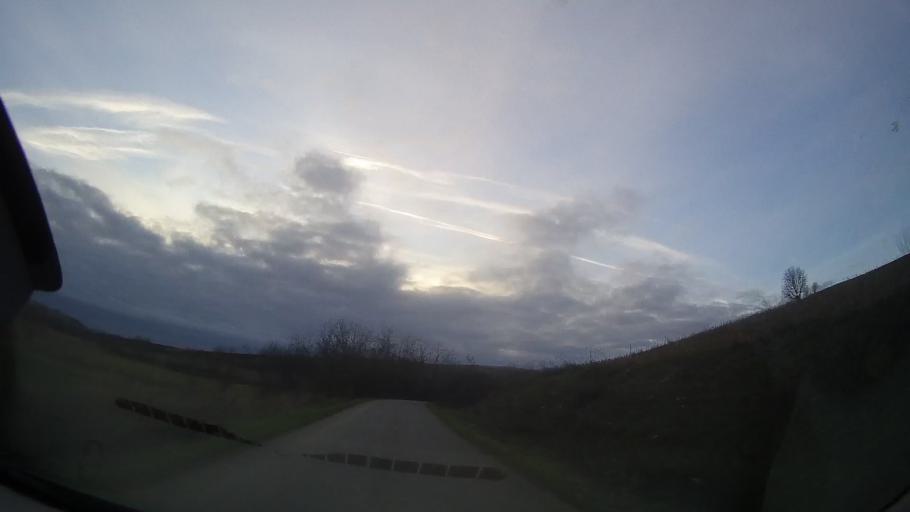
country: RO
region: Cluj
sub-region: Comuna Geaca
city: Geaca
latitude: 46.8520
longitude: 24.0602
